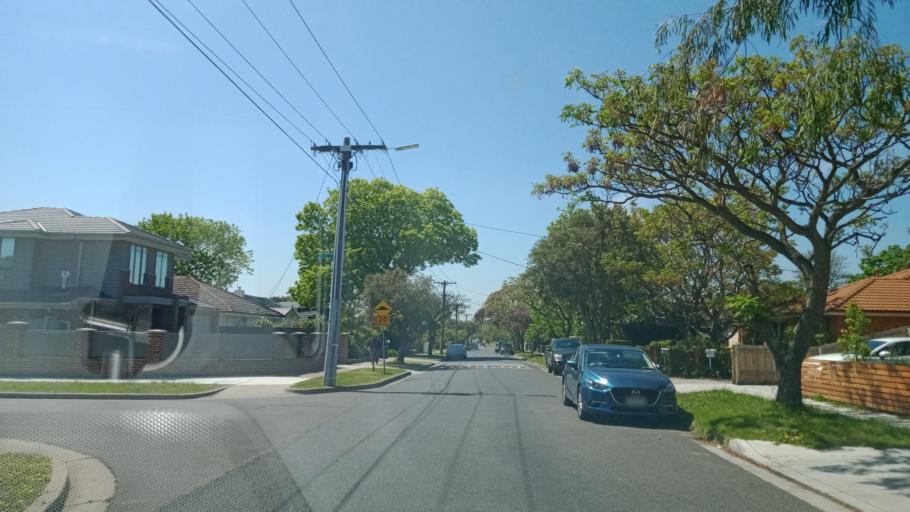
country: AU
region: Victoria
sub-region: Monash
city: Oakleigh South
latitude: -37.9165
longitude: 145.0766
